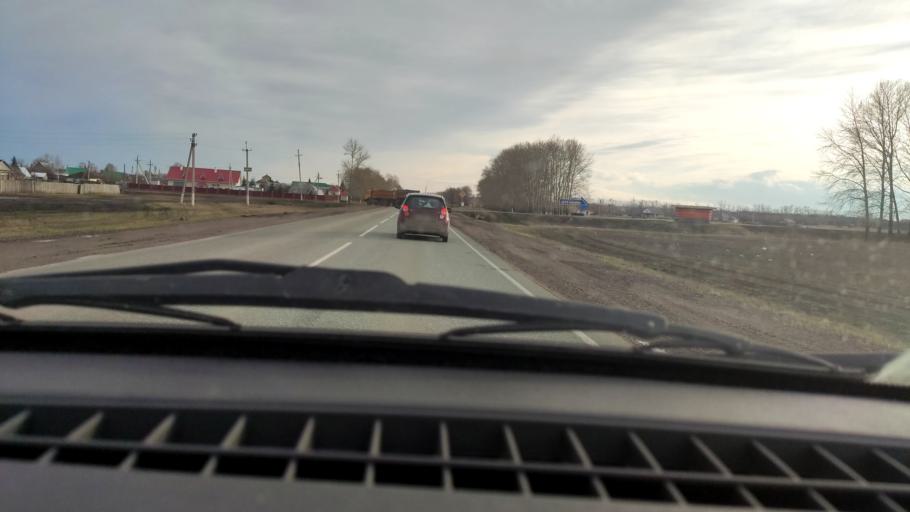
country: RU
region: Bashkortostan
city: Davlekanovo
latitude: 54.3940
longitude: 55.2058
